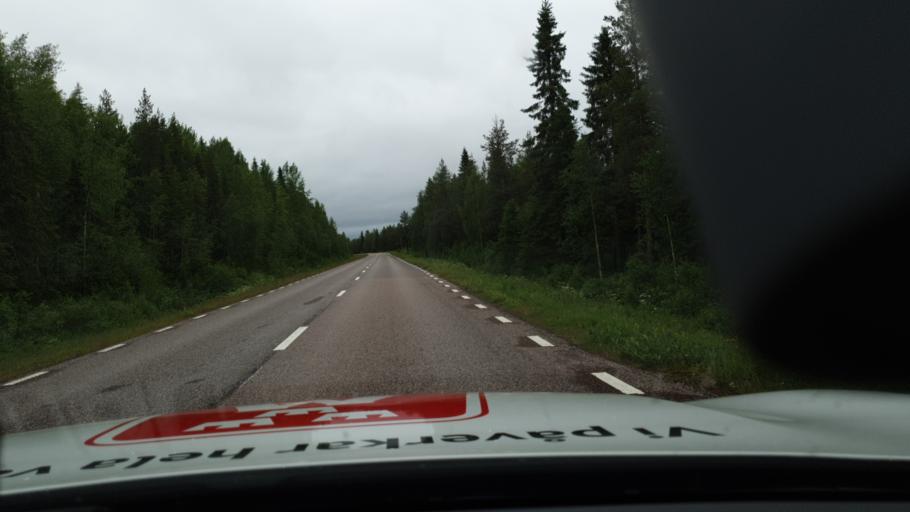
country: FI
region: Lapland
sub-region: Tunturi-Lappi
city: Kolari
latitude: 67.0817
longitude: 23.6606
